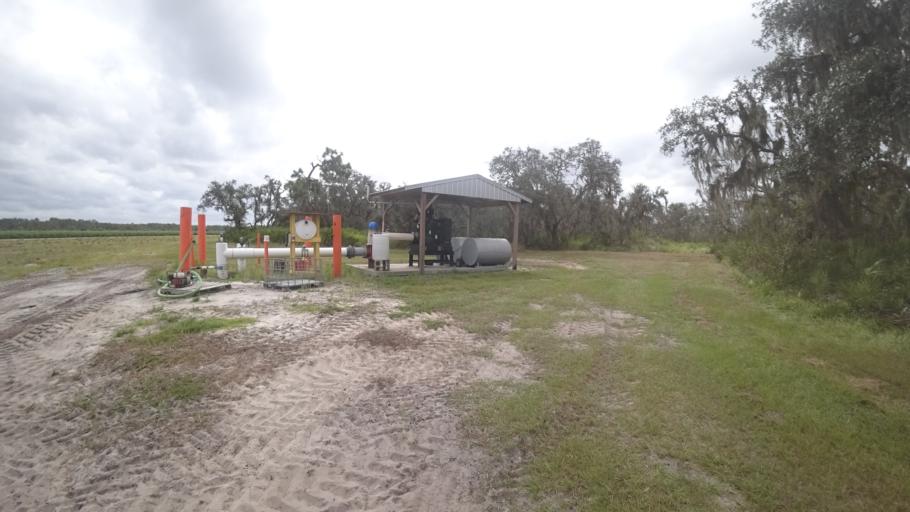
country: US
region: Florida
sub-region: Hillsborough County
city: Wimauma
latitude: 27.5616
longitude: -82.1345
